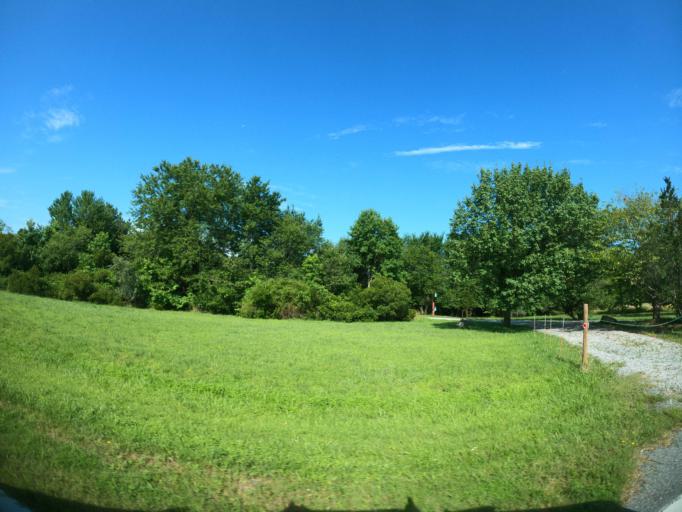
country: US
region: Delaware
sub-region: Sussex County
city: Ocean View
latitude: 38.4850
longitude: -75.1179
